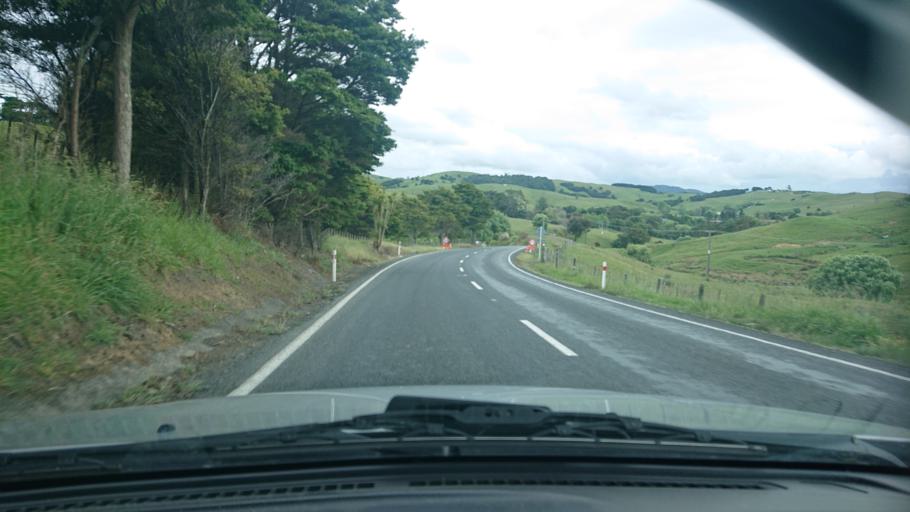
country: NZ
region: Auckland
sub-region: Auckland
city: Wellsford
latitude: -36.3707
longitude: 174.4538
